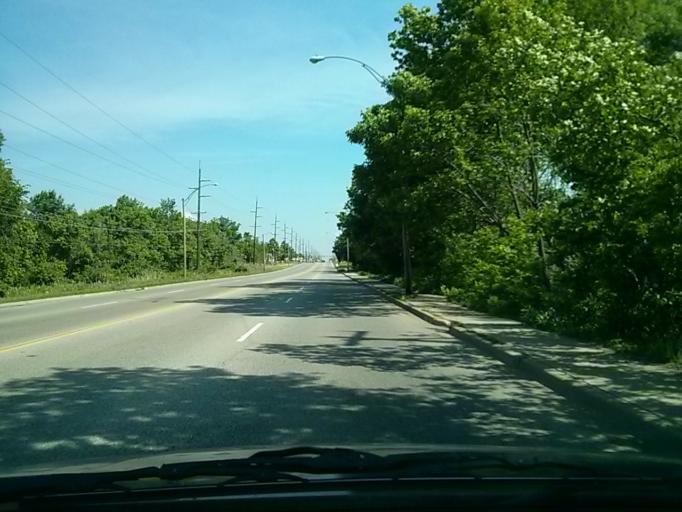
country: US
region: Oklahoma
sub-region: Tulsa County
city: Turley
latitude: 36.2144
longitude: -95.9755
